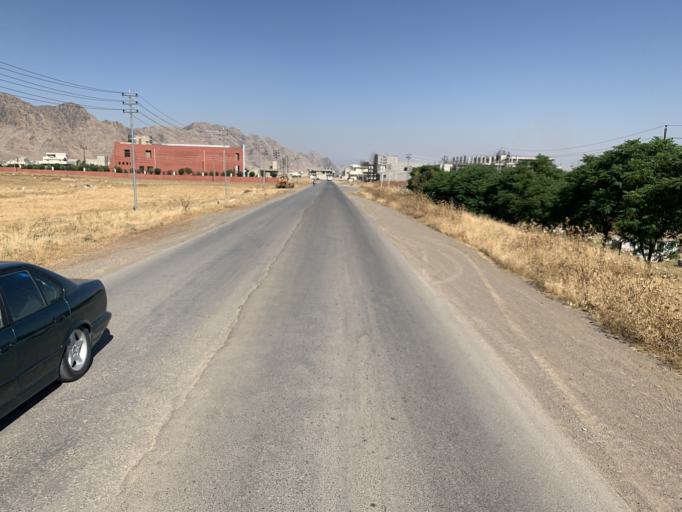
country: IQ
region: As Sulaymaniyah
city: Raniye
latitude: 36.2616
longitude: 44.8538
